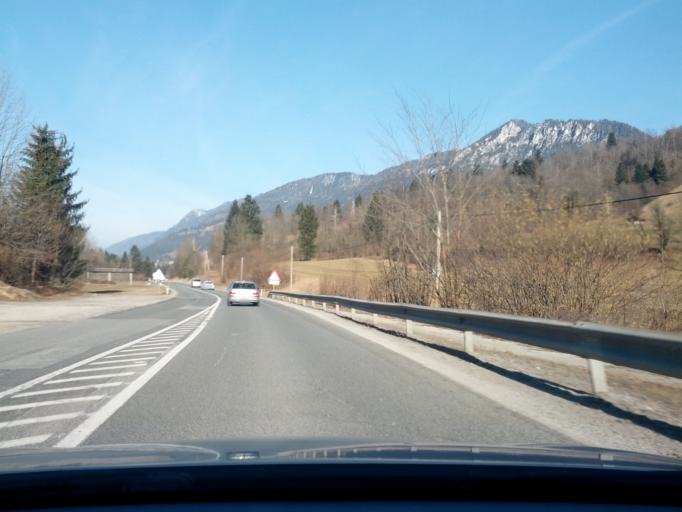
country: SI
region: Jesenice
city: Hrusica
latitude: 46.4572
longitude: 13.9775
